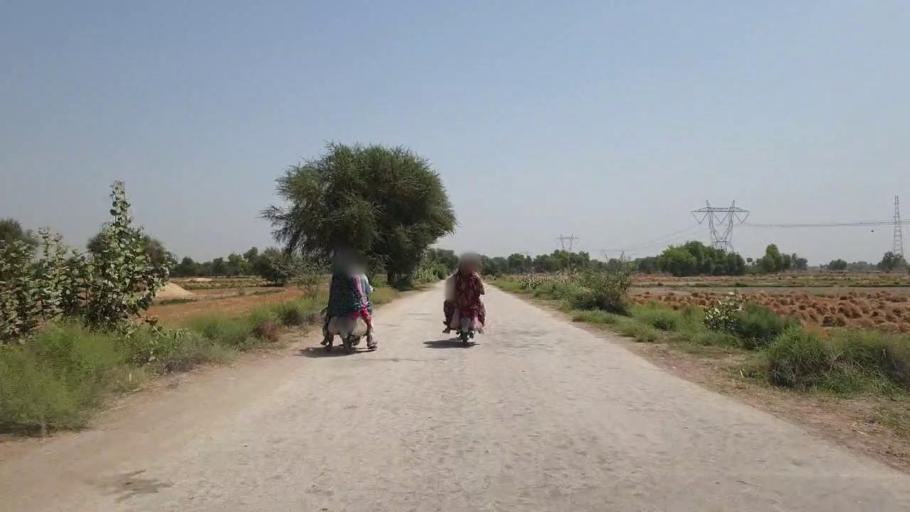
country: PK
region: Sindh
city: Pano Aqil
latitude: 27.8215
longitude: 69.2436
